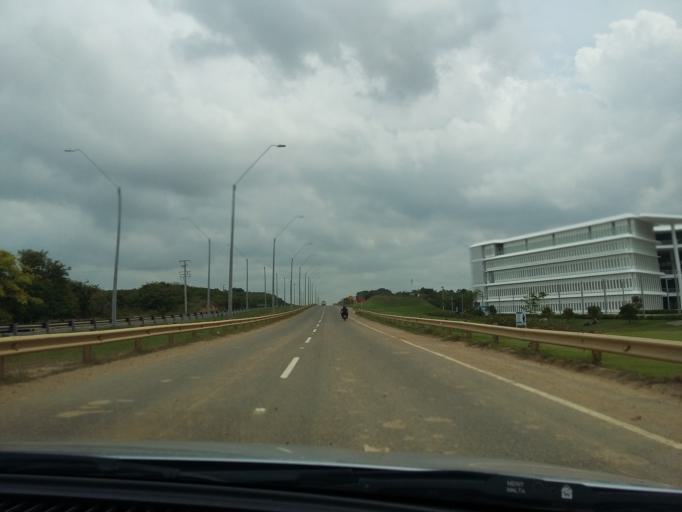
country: CO
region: Bolivar
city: Cartagena
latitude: 10.5065
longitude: -75.4729
